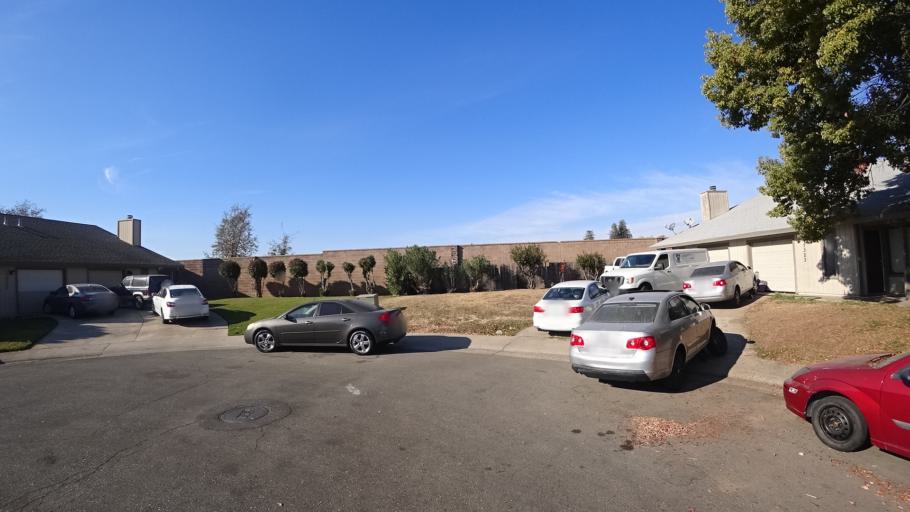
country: US
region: California
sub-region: Sacramento County
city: Citrus Heights
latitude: 38.6920
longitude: -121.2946
